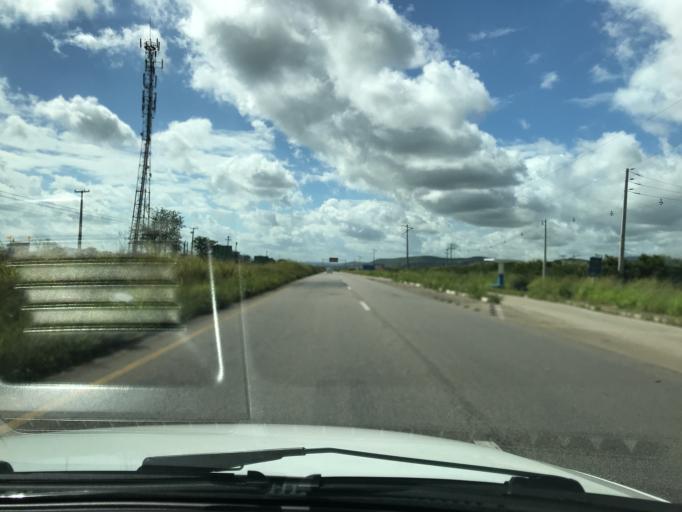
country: BR
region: Pernambuco
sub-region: Gravata
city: Gravata
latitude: -8.2171
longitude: -35.6519
